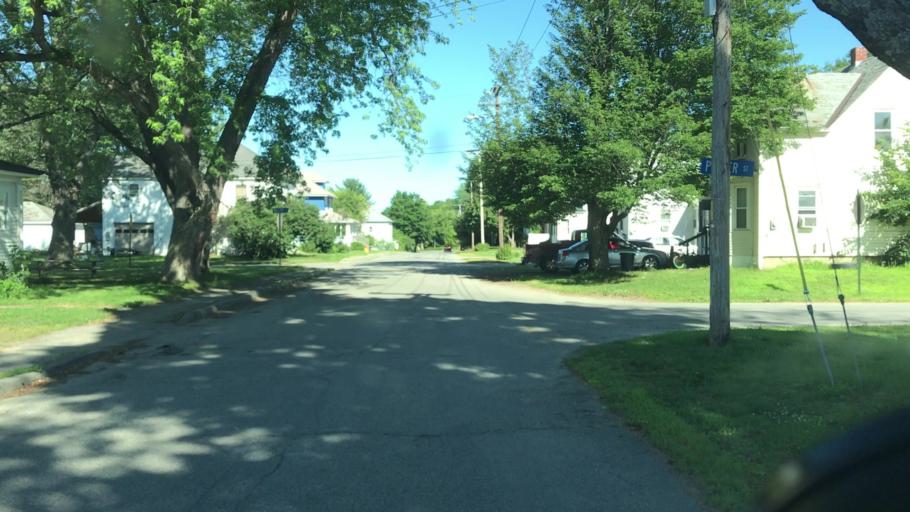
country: US
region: Maine
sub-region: Penobscot County
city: Lincoln
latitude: 45.3665
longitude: -68.4976
